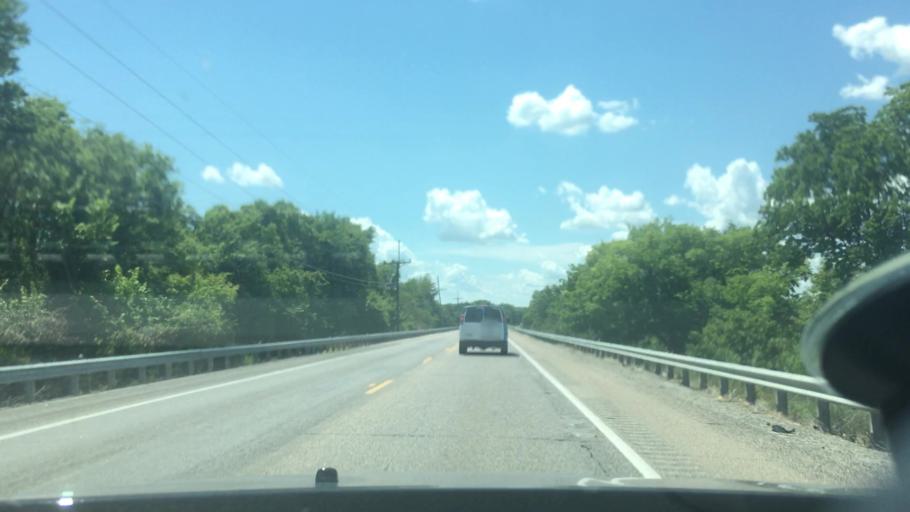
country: US
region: Texas
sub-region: Grayson County
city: Preston
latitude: 33.9983
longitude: -96.5791
